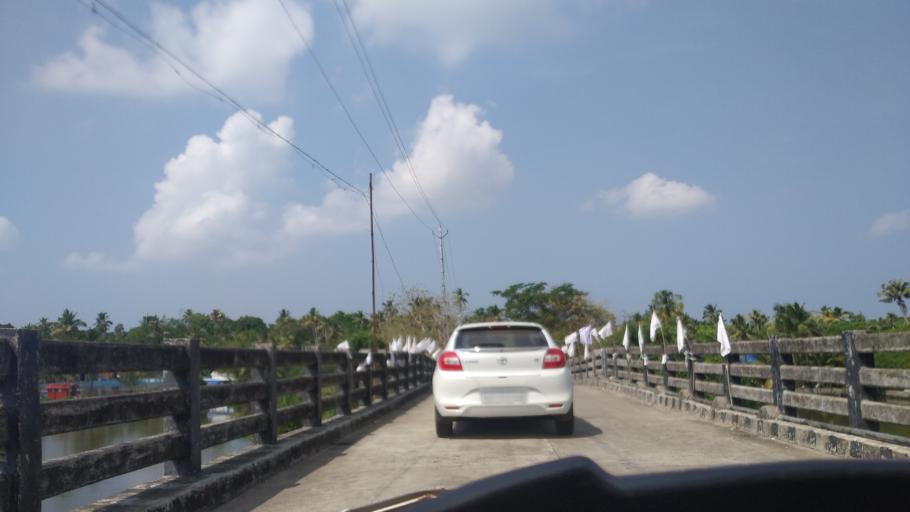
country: IN
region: Kerala
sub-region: Ernakulam
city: Elur
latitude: 10.1131
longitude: 76.2316
